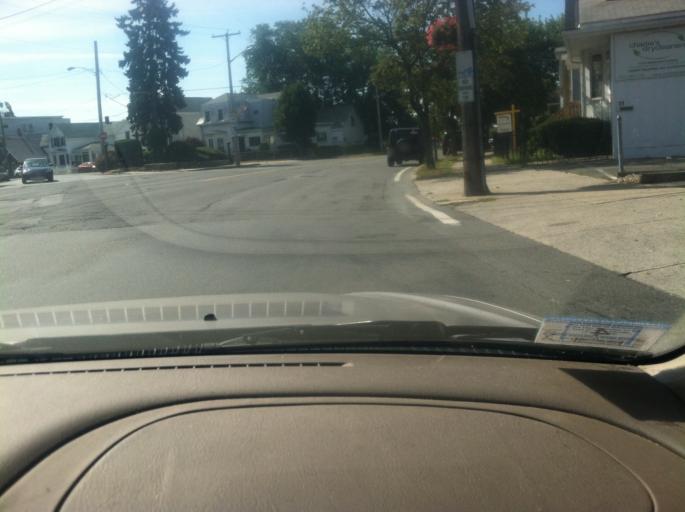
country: US
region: Massachusetts
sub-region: Suffolk County
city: Revere
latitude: 42.3972
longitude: -70.9921
